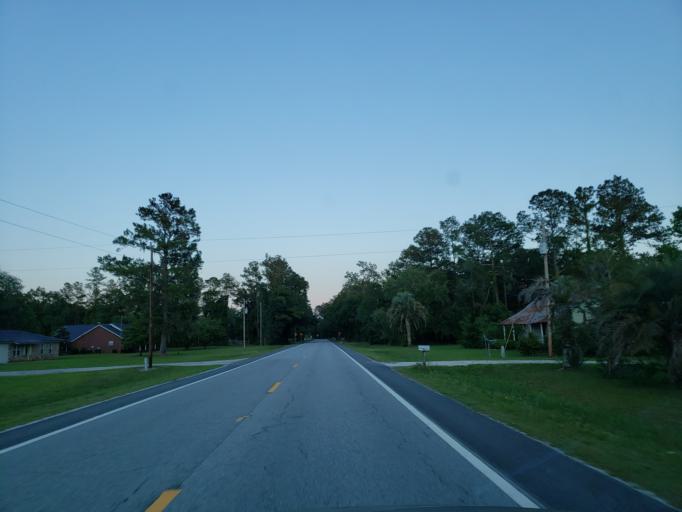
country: US
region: Florida
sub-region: Hamilton County
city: Jasper
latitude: 30.5529
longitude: -83.0665
